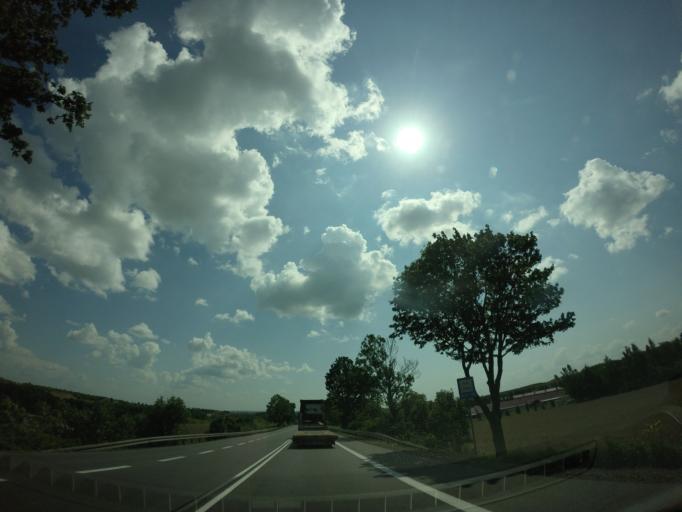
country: PL
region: Podlasie
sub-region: Powiat lomzynski
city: Piatnica
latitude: 53.2065
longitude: 22.1023
